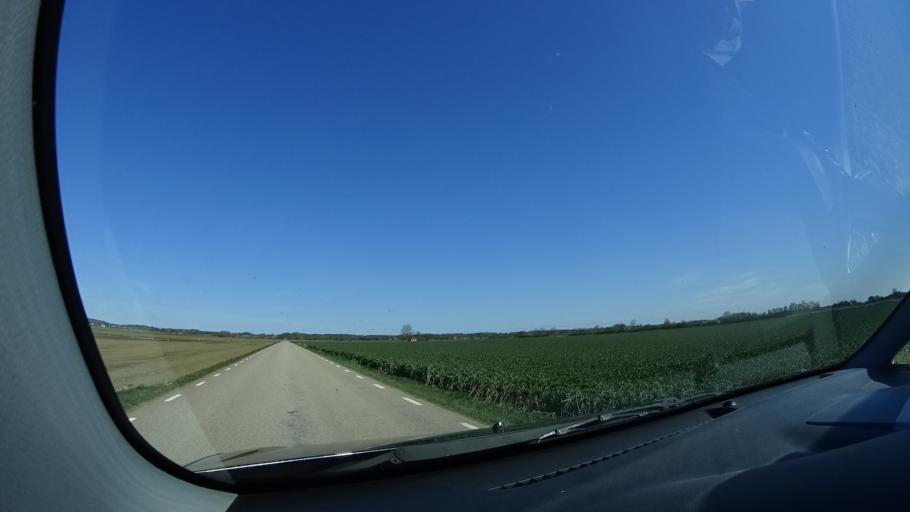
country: SE
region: Skane
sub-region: Hoganas Kommun
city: Hoganas
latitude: 56.2342
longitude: 12.5862
